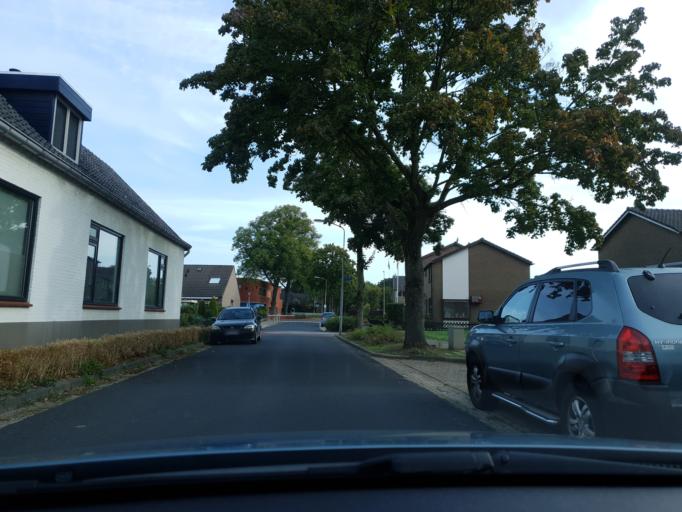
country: NL
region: Gelderland
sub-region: Gemeente Overbetuwe
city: Oosterhout
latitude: 51.8560
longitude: 5.8107
